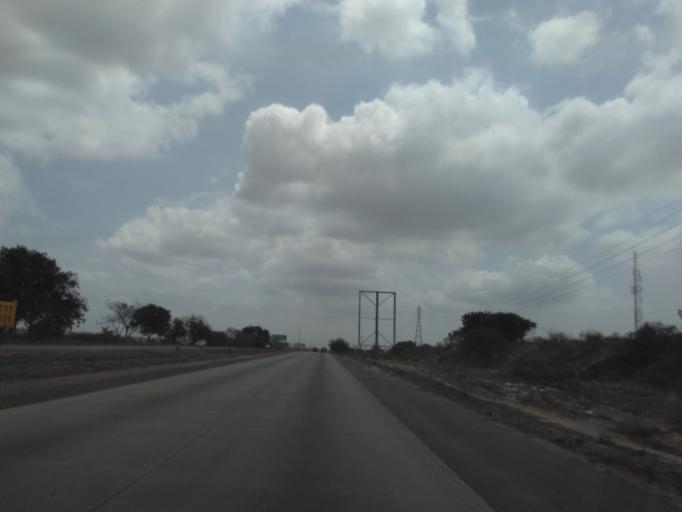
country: GH
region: Greater Accra
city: Tema
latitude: 5.6752
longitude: -0.0431
